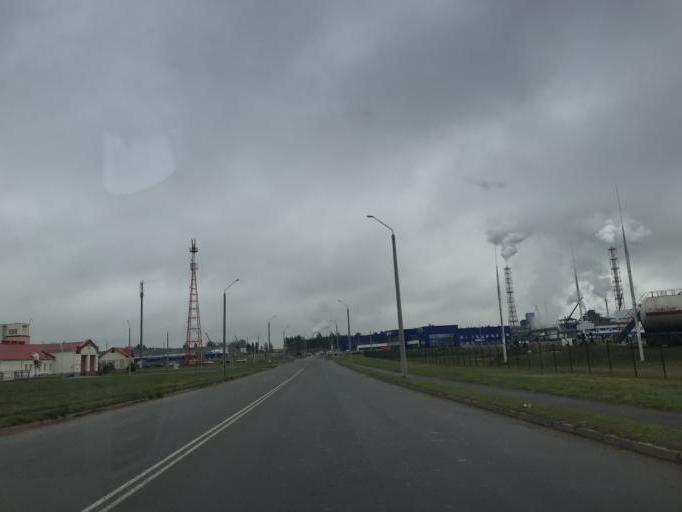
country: BY
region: Mogilev
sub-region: Mahilyowski Rayon
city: Veyno
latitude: 53.8288
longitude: 30.3491
